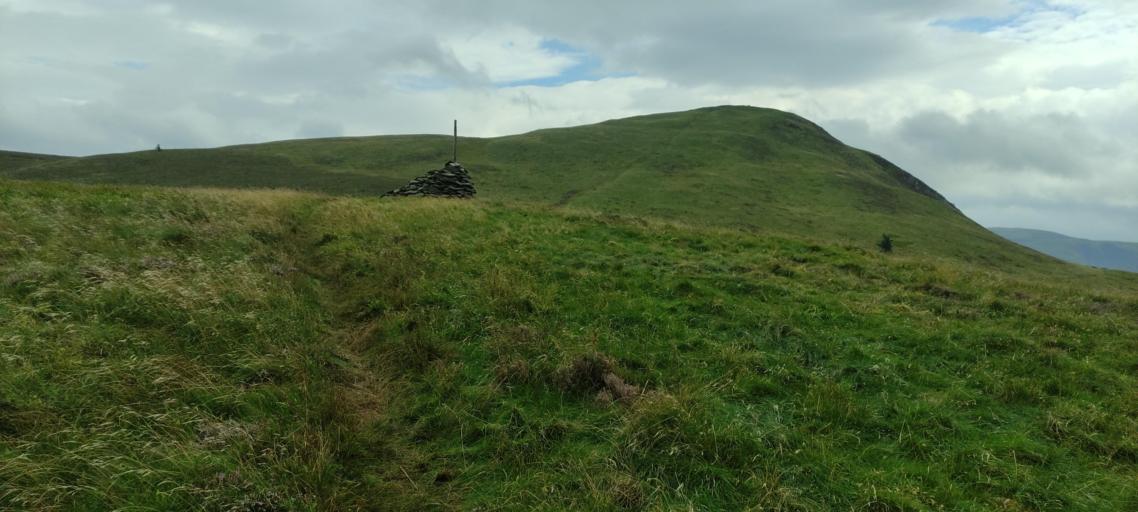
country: GB
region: England
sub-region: Cumbria
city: Cockermouth
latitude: 54.5683
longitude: -3.3831
